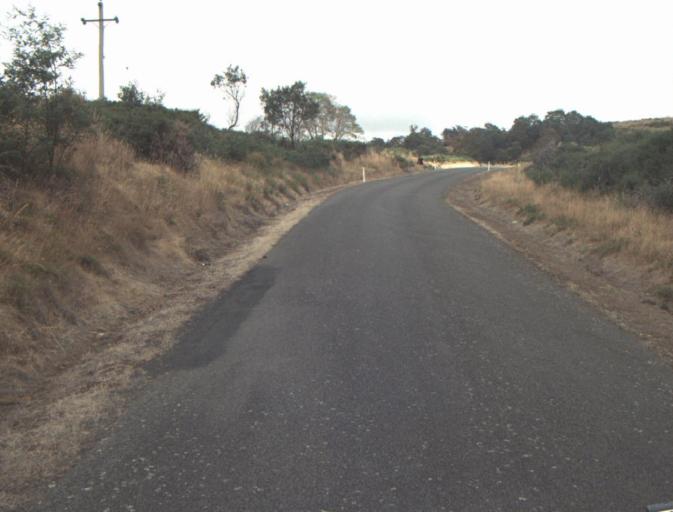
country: AU
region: Tasmania
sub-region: Northern Midlands
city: Evandale
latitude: -41.5123
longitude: 147.4742
